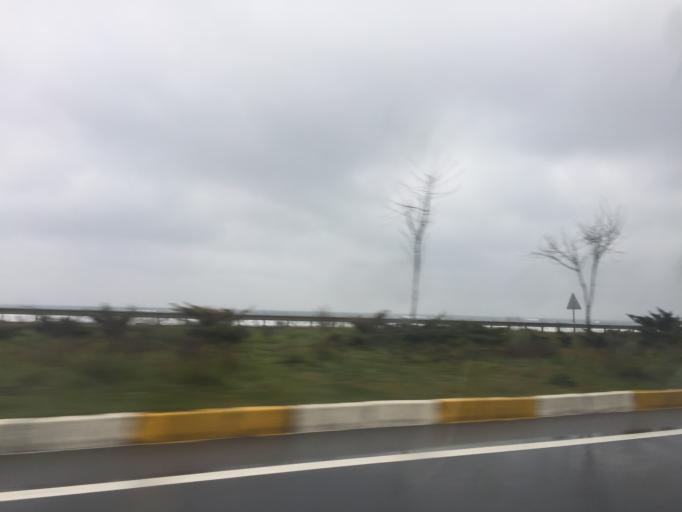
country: TR
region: Duzce
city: Akcakoca
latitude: 41.1035
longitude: 31.2508
